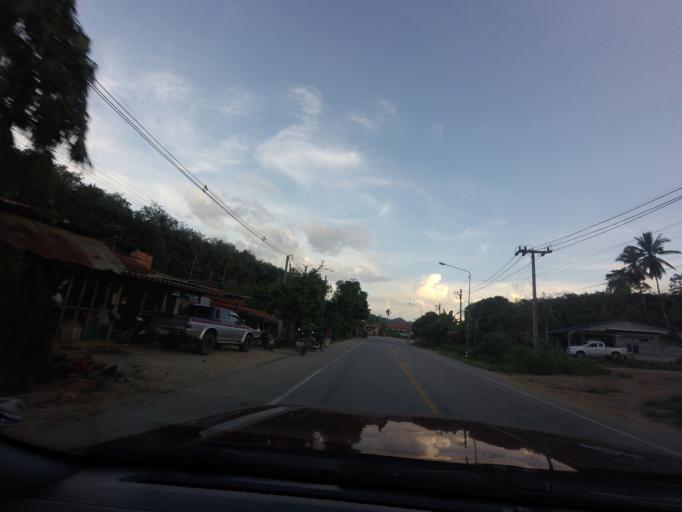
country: TH
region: Yala
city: Than To
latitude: 6.1196
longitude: 101.1913
